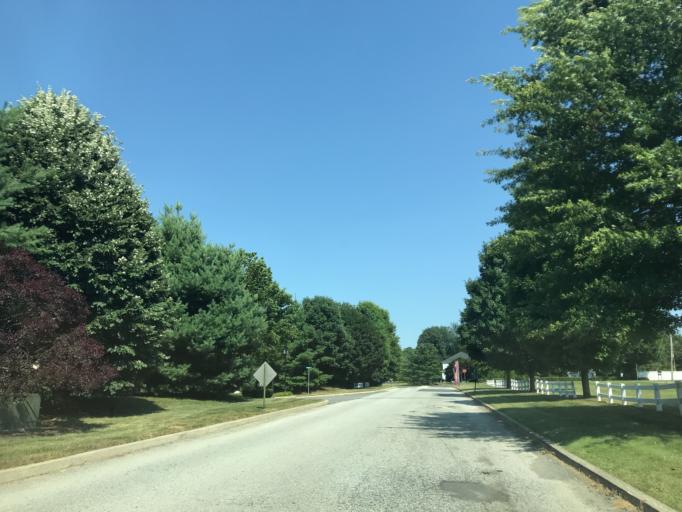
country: US
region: Pennsylvania
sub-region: Delaware County
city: Chester Heights
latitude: 39.8370
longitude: -75.5202
